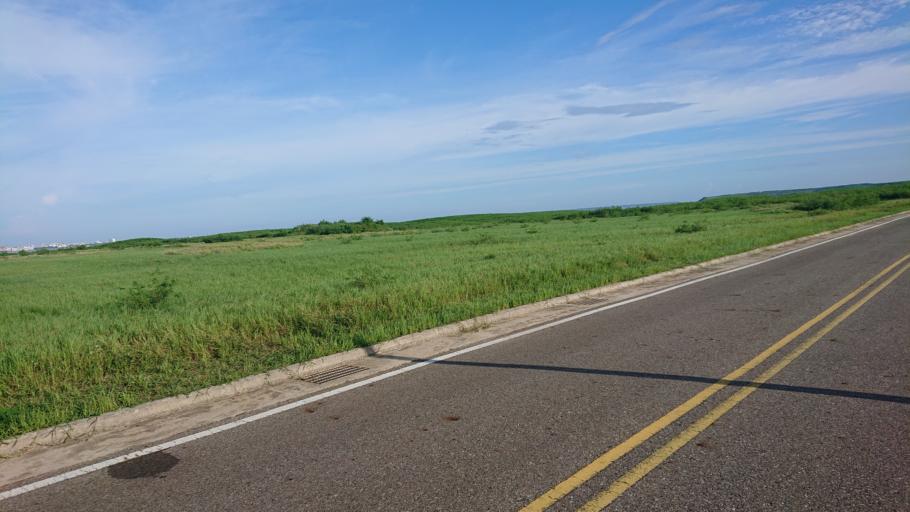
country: TW
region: Taiwan
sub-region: Penghu
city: Ma-kung
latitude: 23.6001
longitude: 119.5180
